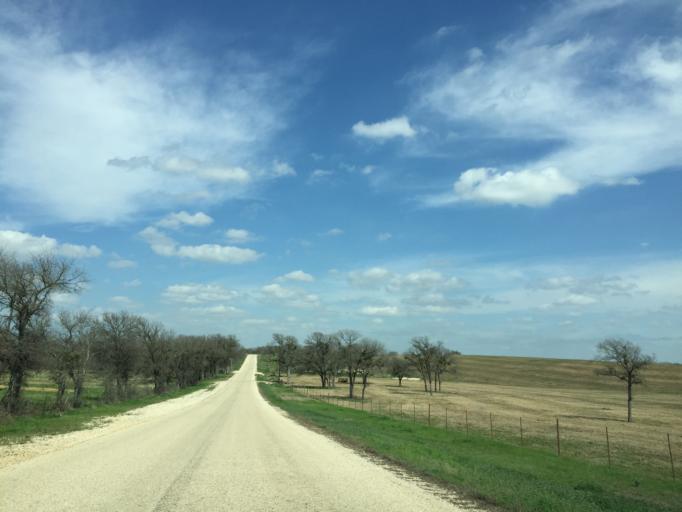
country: US
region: Texas
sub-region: Milam County
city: Thorndale
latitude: 30.5548
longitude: -97.2168
